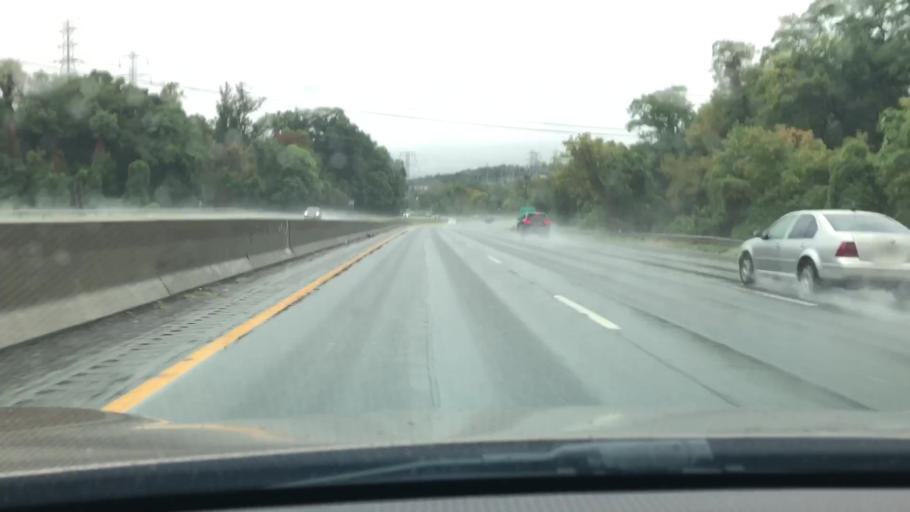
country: US
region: New York
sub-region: Westchester County
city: Bronxville
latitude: 40.9481
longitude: -73.8511
